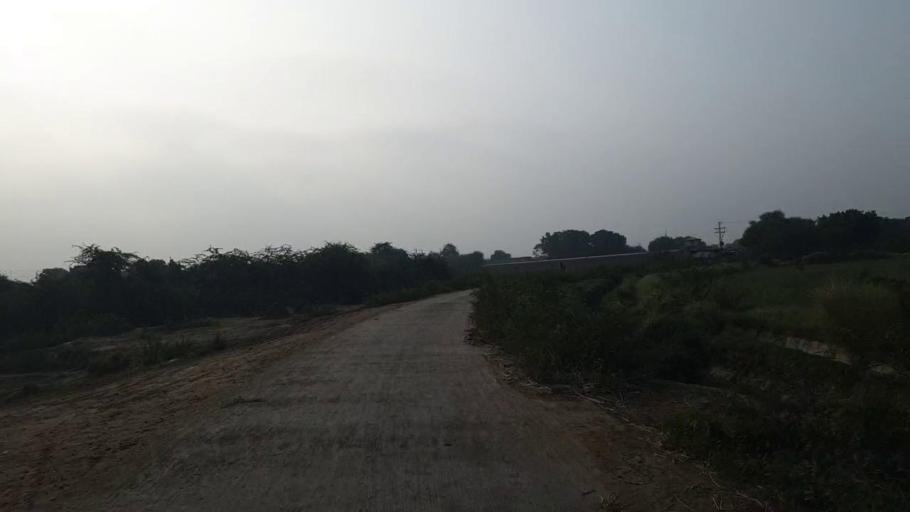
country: PK
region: Sindh
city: Tando Muhammad Khan
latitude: 25.1676
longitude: 68.6111
